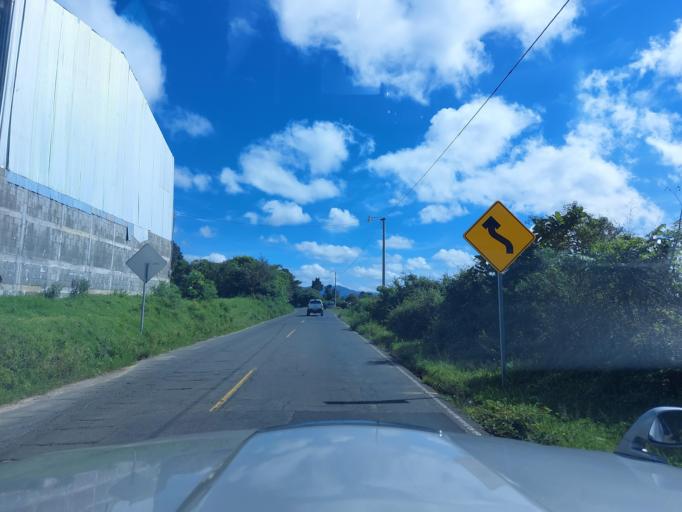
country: GT
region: Chimaltenango
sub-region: Municipio de Zaragoza
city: Zaragoza
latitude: 14.6563
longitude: -90.8970
